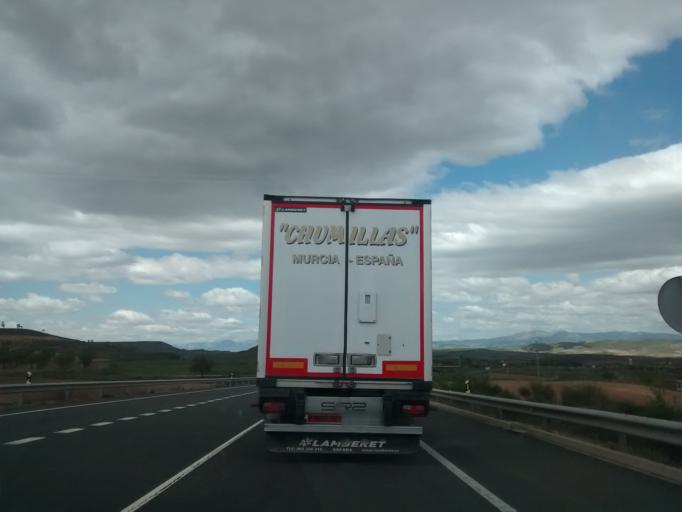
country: ES
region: La Rioja
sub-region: Provincia de La Rioja
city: Ausejo
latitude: 42.3398
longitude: -2.1744
